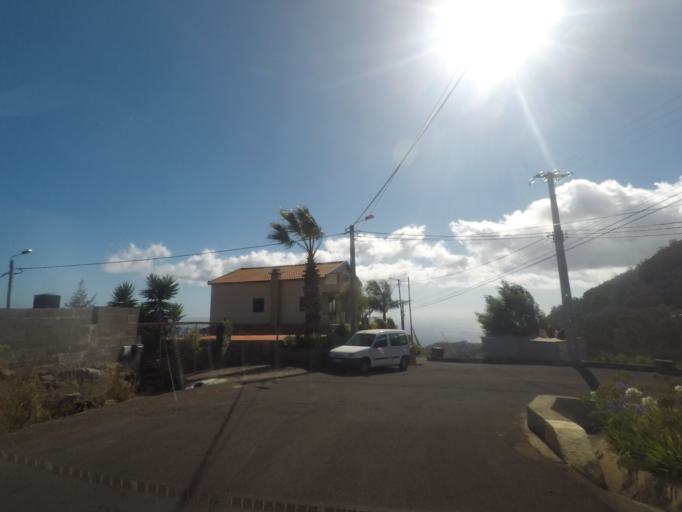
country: PT
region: Madeira
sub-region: Ribeira Brava
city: Campanario
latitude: 32.6817
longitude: -17.0244
